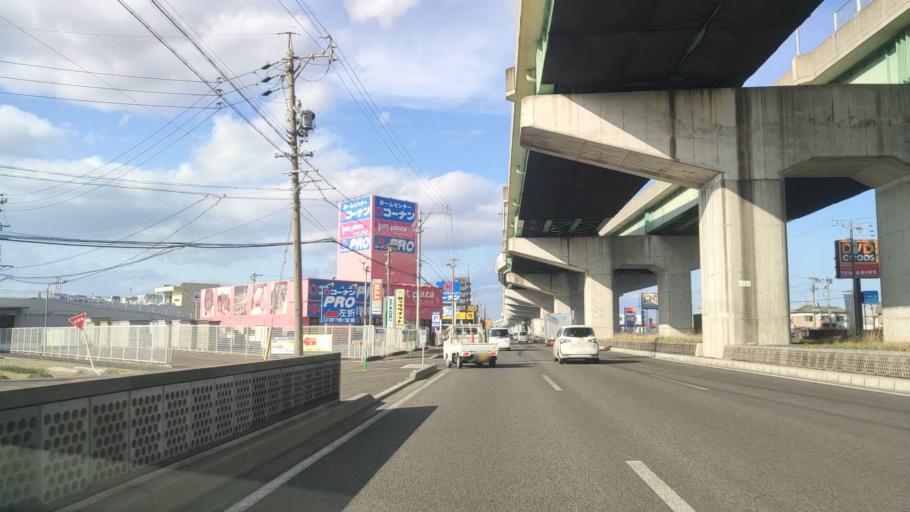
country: JP
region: Aichi
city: Ichinomiya
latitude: 35.2791
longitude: 136.8298
